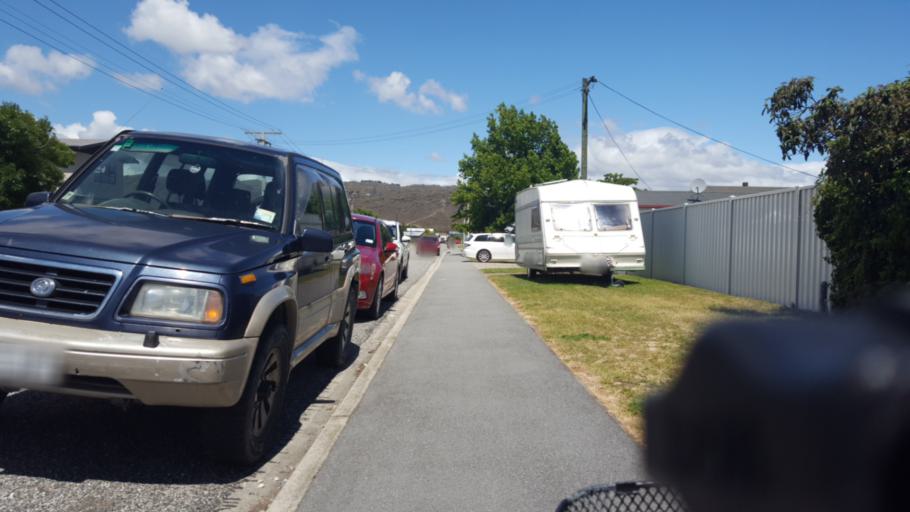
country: NZ
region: Otago
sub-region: Queenstown-Lakes District
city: Wanaka
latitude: -45.2448
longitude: 169.3904
